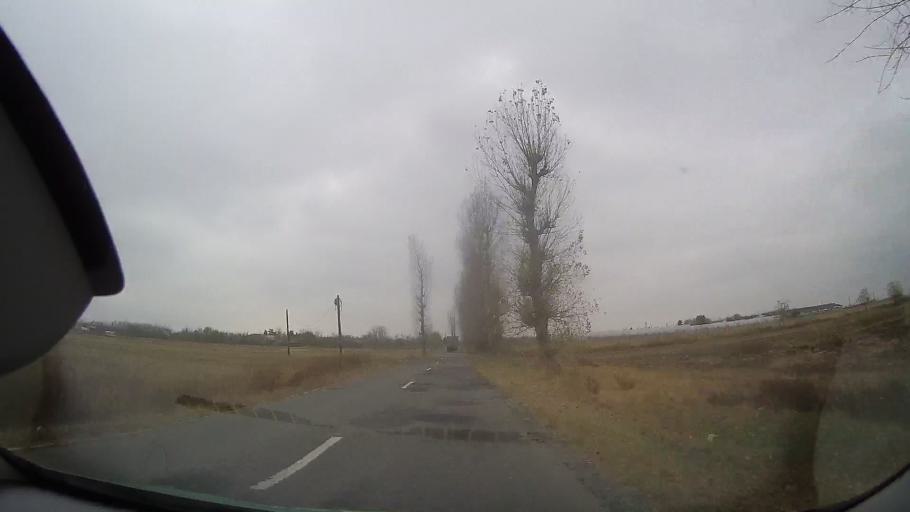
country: RO
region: Ialomita
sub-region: Comuna Valea Macrisului
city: Valea Macrisului
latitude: 44.7384
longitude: 26.8440
